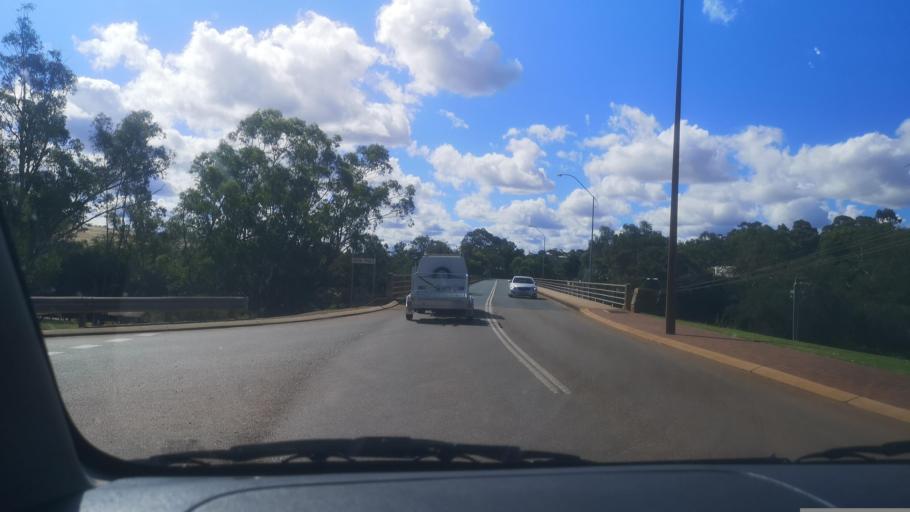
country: AU
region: Western Australia
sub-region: Toodyay
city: Toodyay
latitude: -31.5501
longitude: 116.4639
